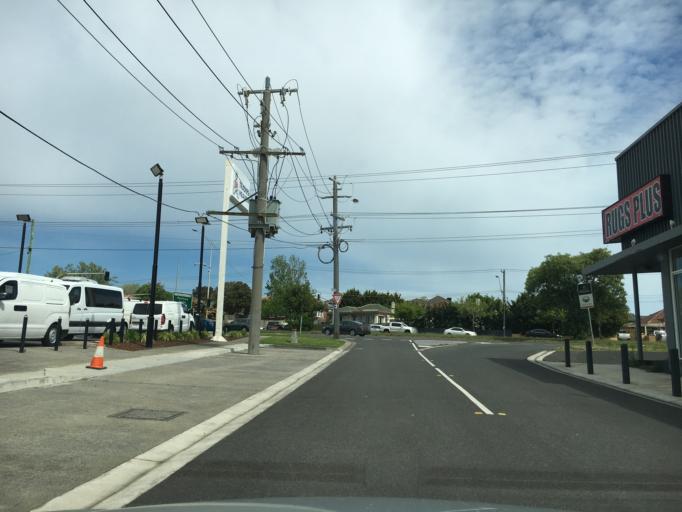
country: AU
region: Victoria
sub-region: Monash
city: Chadstone
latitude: -37.8956
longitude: 145.0981
